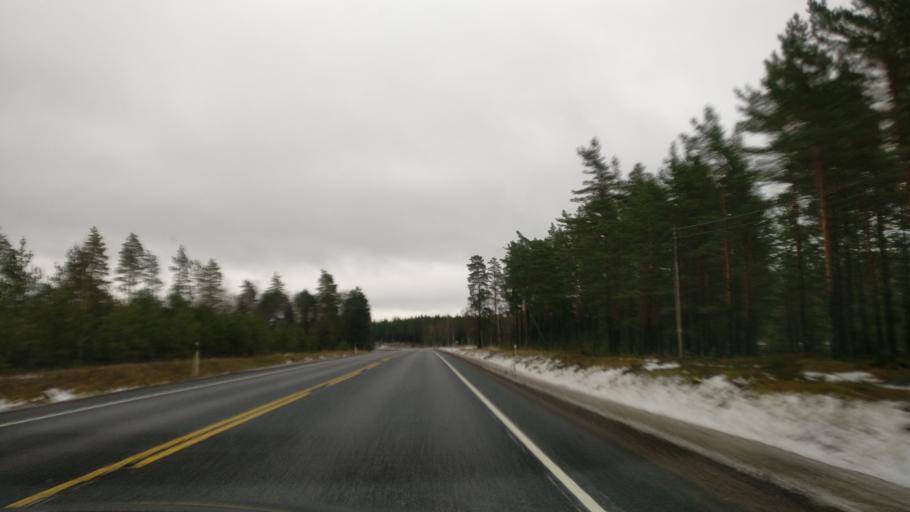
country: FI
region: Uusimaa
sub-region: Raaseporin
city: Ekenaes
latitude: 59.9311
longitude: 23.3222
